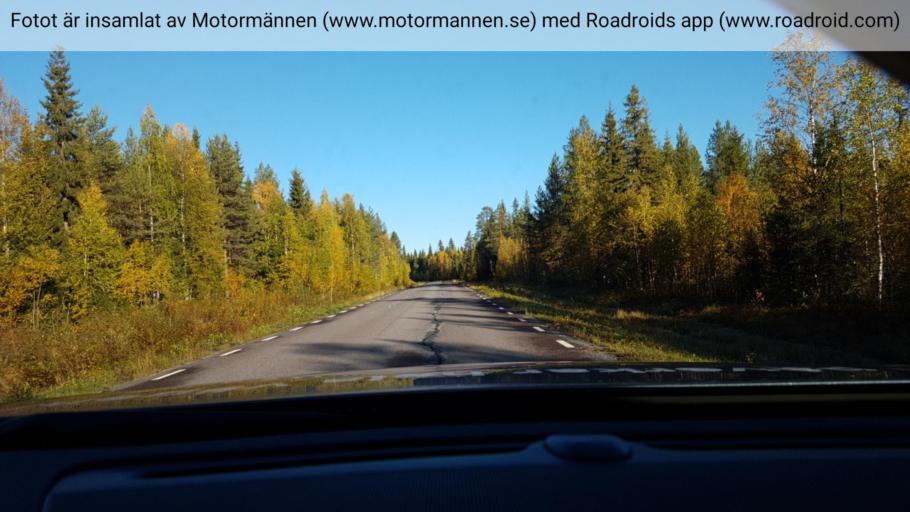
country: SE
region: Norrbotten
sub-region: Bodens Kommun
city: Boden
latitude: 66.0008
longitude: 21.5814
